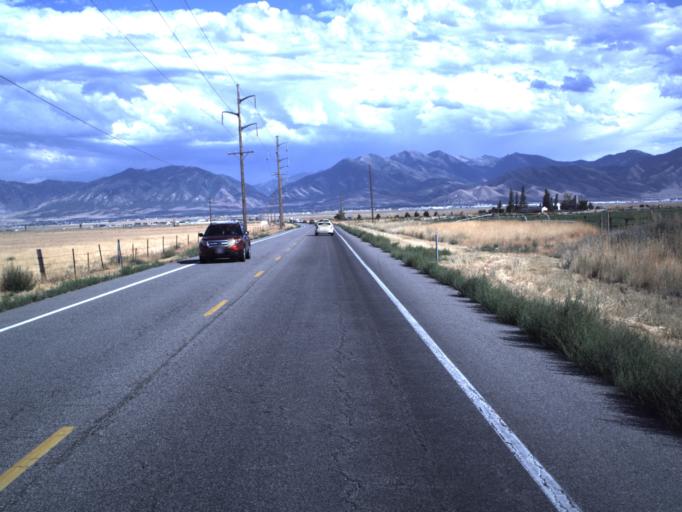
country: US
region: Utah
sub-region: Tooele County
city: Grantsville
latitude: 40.5890
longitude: -112.4169
